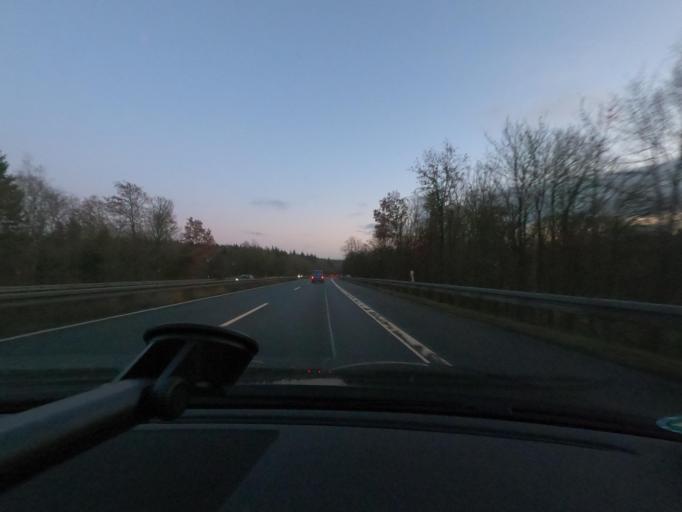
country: DE
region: Lower Saxony
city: Hoerden
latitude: 51.6905
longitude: 10.2971
